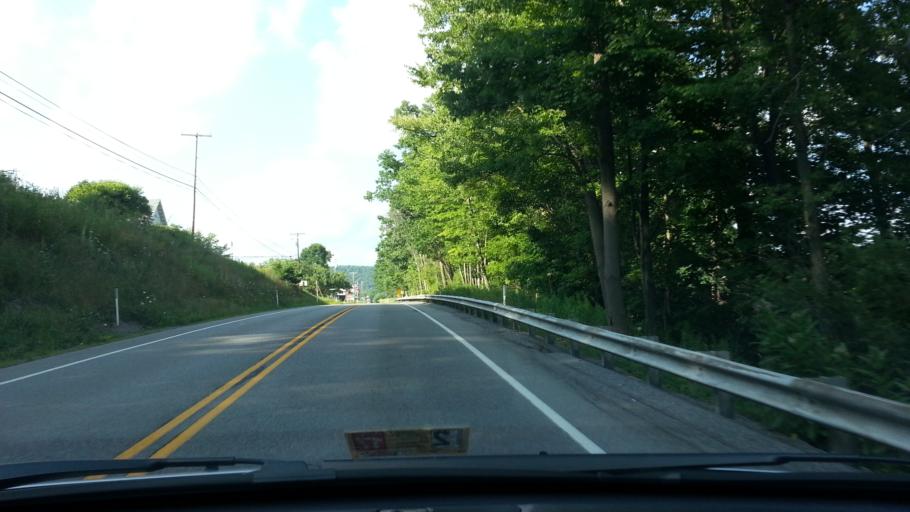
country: US
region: Pennsylvania
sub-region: Elk County
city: Saint Marys
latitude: 41.2614
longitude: -78.5008
